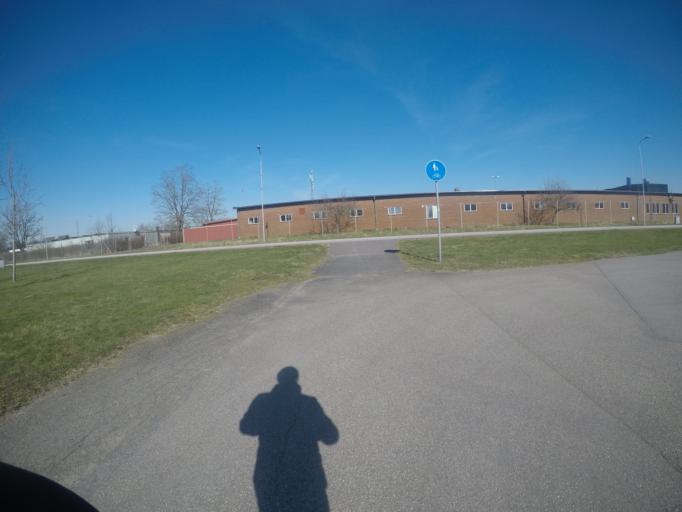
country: SE
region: Halland
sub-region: Laholms Kommun
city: Laholm
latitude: 56.5076
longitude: 13.0556
